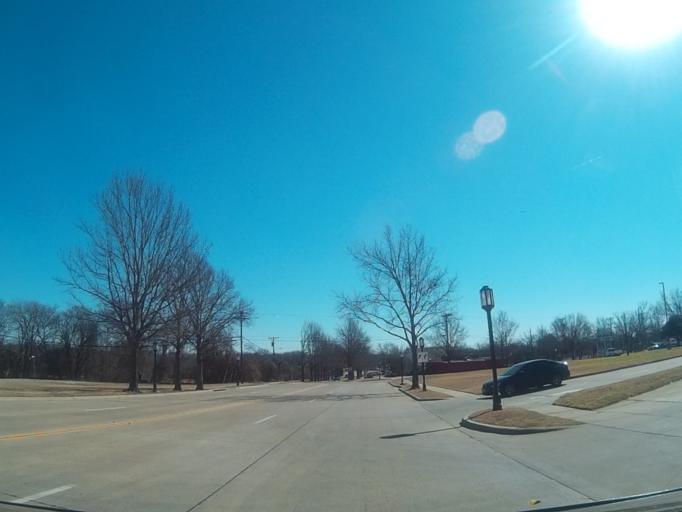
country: US
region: Texas
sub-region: Collin County
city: Allen
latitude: 33.1019
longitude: -96.6657
